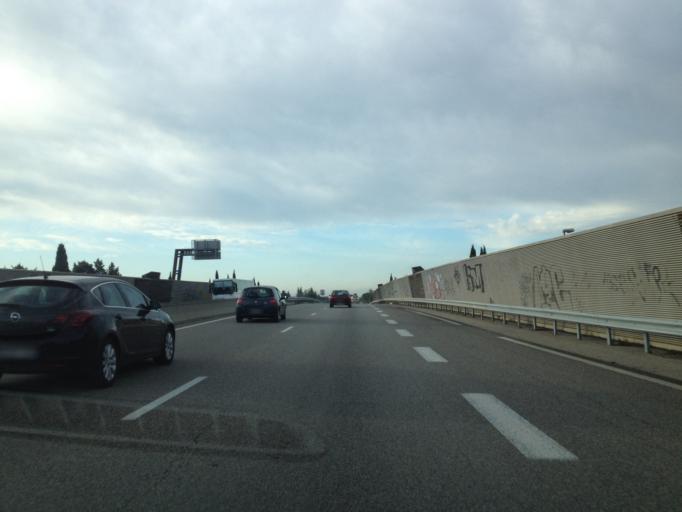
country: FR
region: Provence-Alpes-Cote d'Azur
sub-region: Departement du Vaucluse
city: Sorgues
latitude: 44.0154
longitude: 4.8676
